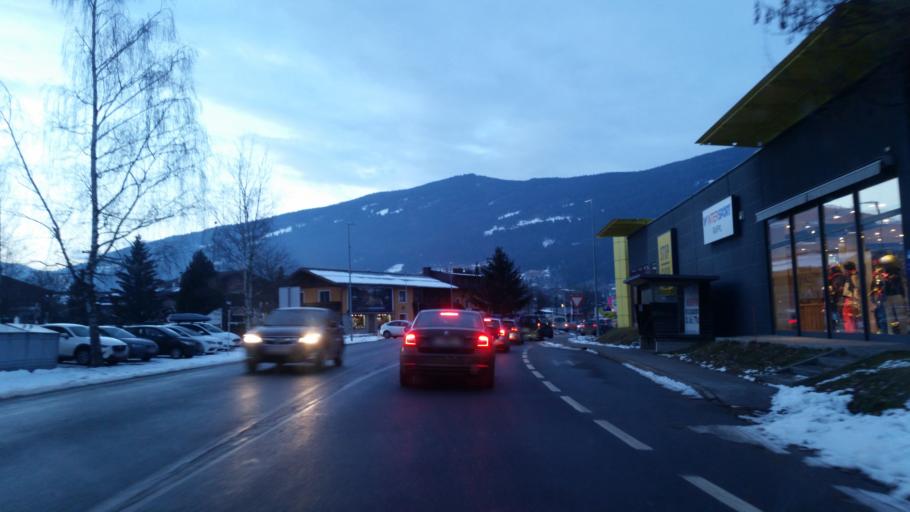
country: AT
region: Salzburg
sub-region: Politischer Bezirk Sankt Johann im Pongau
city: Radstadt
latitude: 47.3773
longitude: 13.4744
